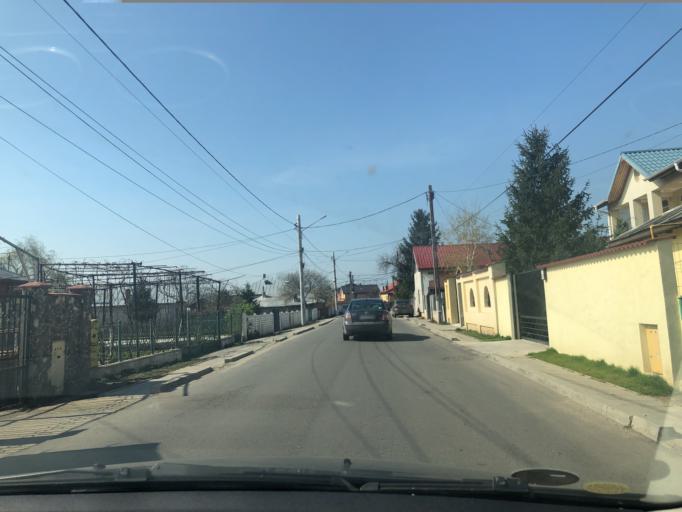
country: RO
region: Ilfov
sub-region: Comuna Clinceni
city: Clinceni
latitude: 44.3731
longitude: 25.9588
